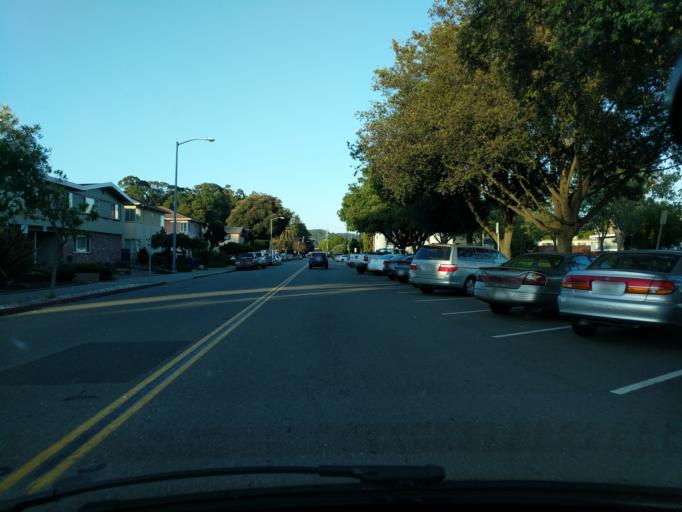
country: US
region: California
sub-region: Alameda County
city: San Leandro
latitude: 37.7267
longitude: -122.1535
